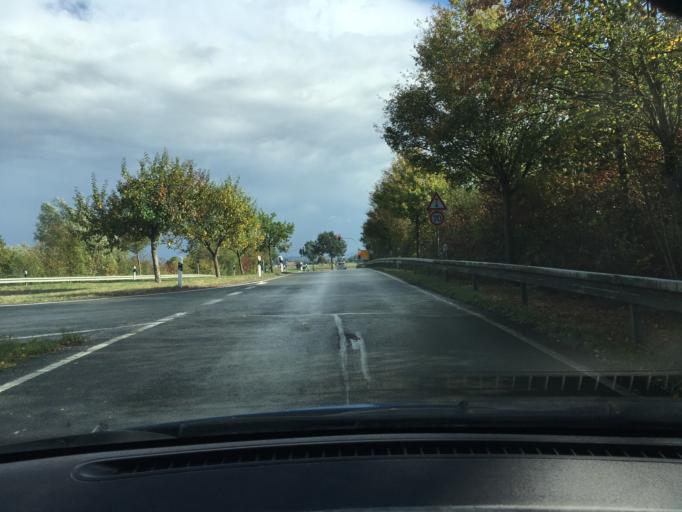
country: DE
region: Lower Saxony
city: Springe
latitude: 52.2116
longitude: 9.5897
